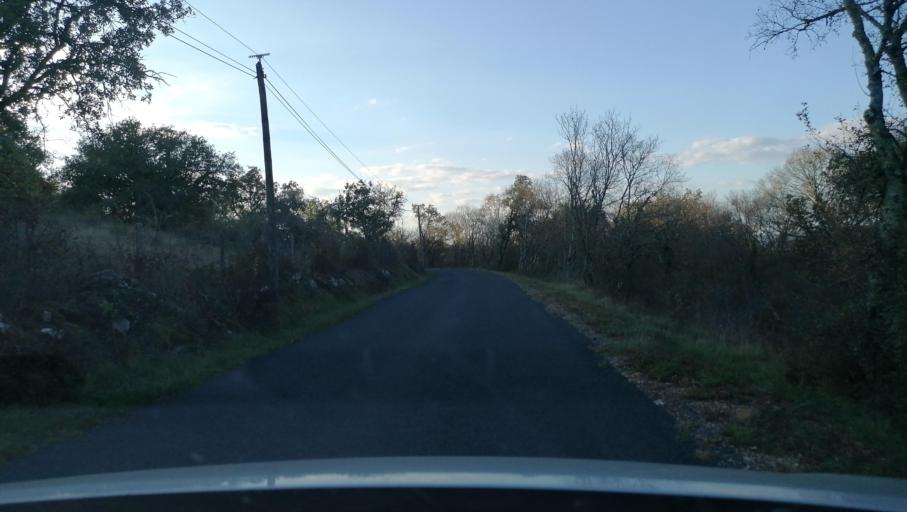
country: FR
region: Midi-Pyrenees
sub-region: Departement du Lot
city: Vayrac
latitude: 44.8701
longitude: 1.6500
